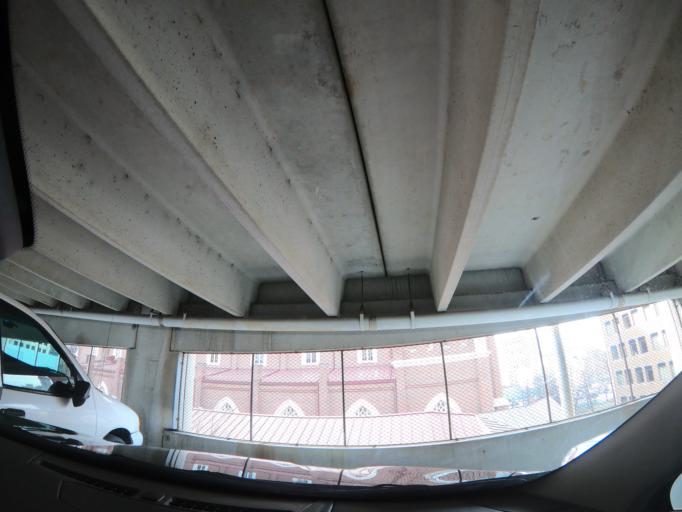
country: US
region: Kentucky
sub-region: Jefferson County
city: Louisville
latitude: 38.2483
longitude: -85.7764
